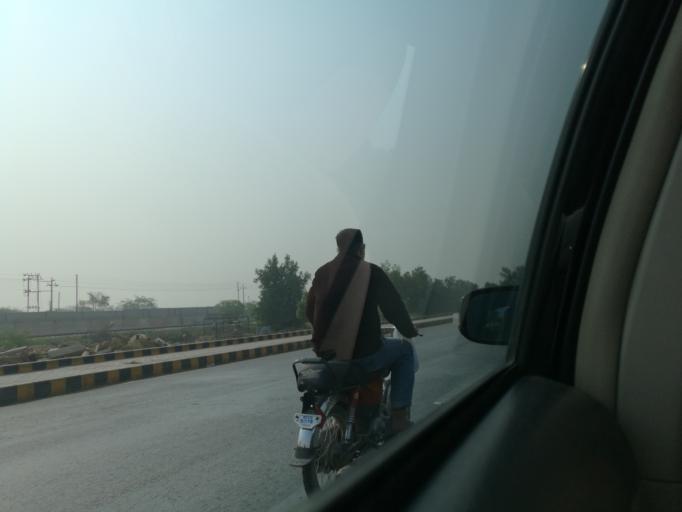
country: PK
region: Sindh
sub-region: Karachi District
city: Karachi
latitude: 24.8823
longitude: 67.1126
